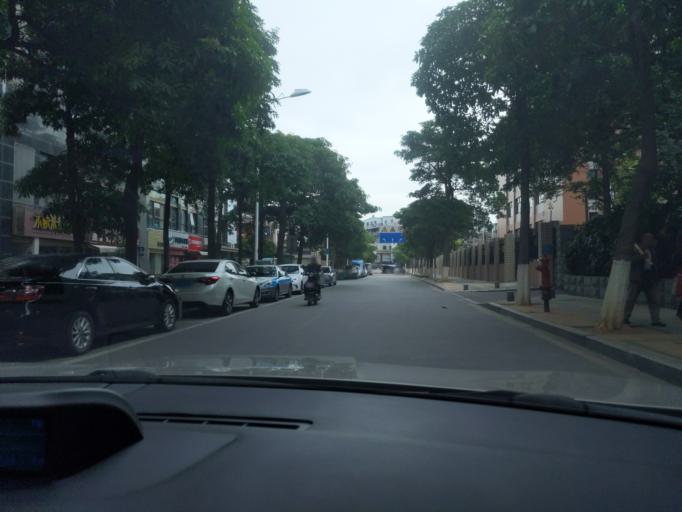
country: CN
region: Fujian
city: Liuwudian
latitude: 24.4868
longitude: 118.1598
